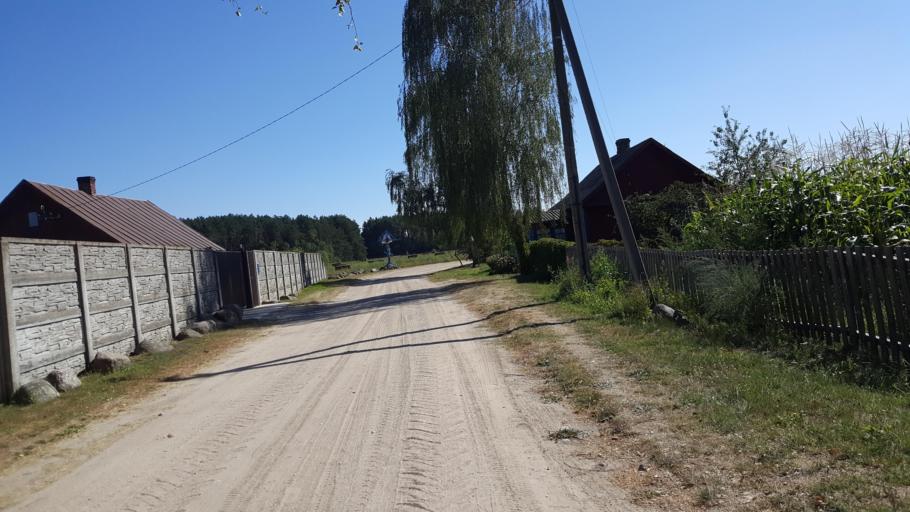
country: PL
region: Lublin Voivodeship
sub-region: Powiat bialski
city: Rokitno
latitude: 52.2182
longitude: 23.3428
